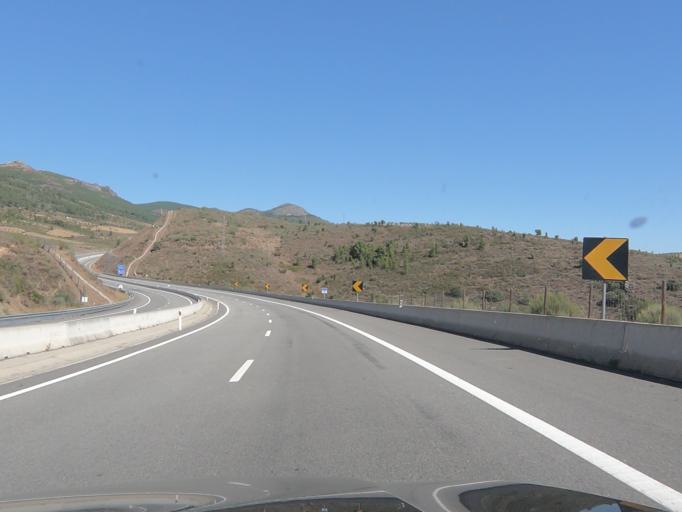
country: PT
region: Vila Real
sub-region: Murca
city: Murca
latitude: 41.4238
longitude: -7.3629
